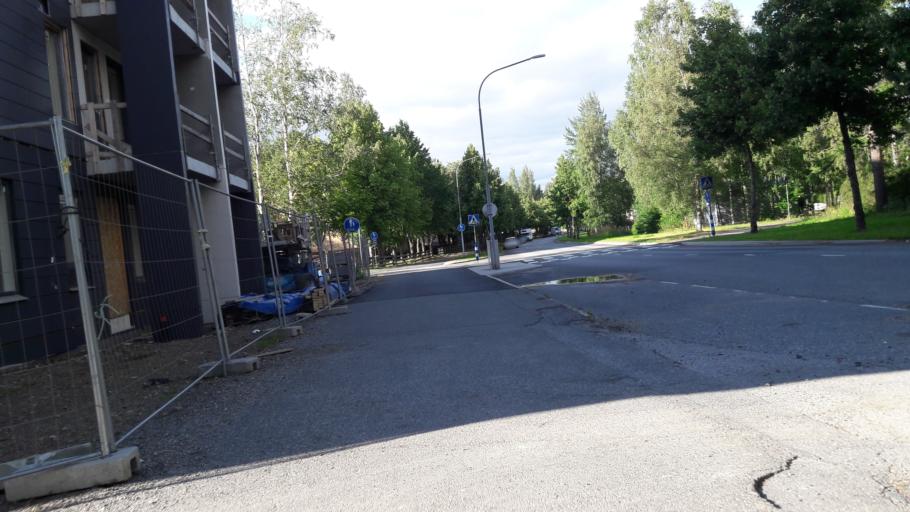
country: FI
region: North Karelia
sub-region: Joensuu
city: Joensuu
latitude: 62.6041
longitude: 29.8041
